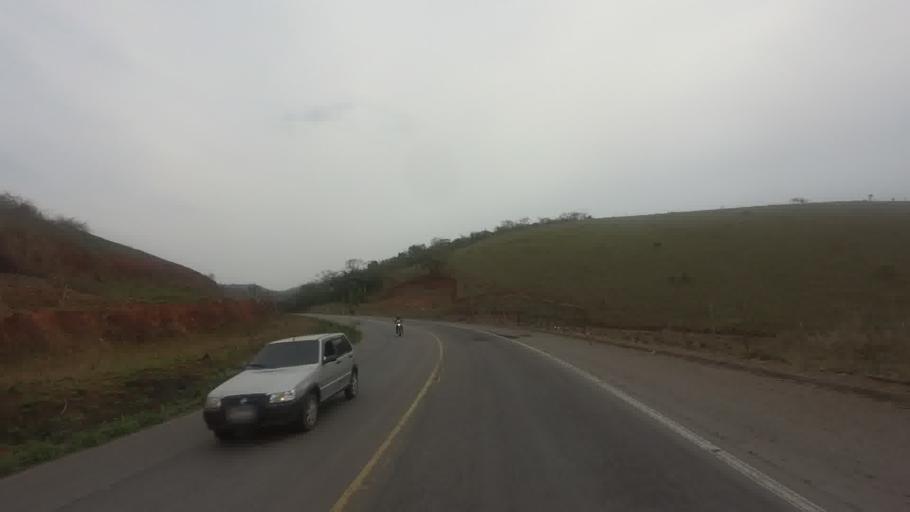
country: BR
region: Rio de Janeiro
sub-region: Santo Antonio De Padua
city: Santo Antonio de Padua
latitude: -21.5766
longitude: -42.2152
